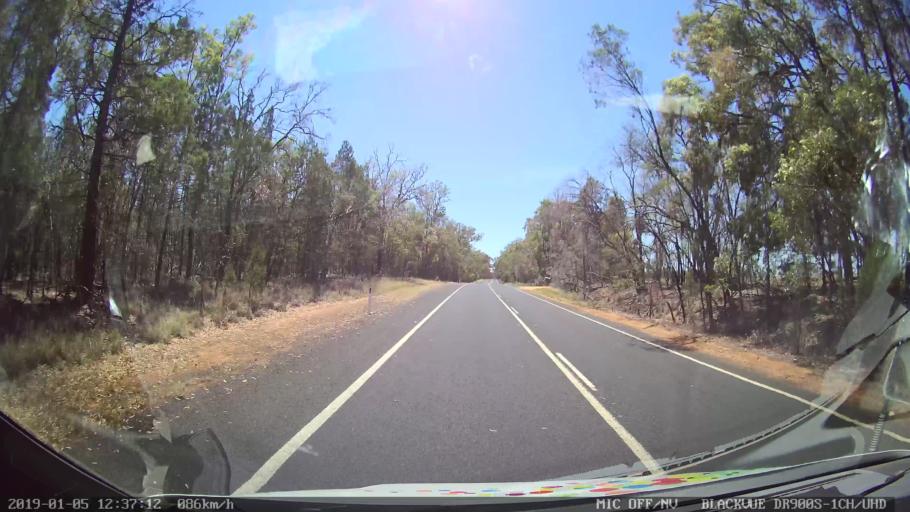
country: AU
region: New South Wales
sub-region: Warrumbungle Shire
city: Coonabarabran
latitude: -31.2044
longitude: 149.4514
